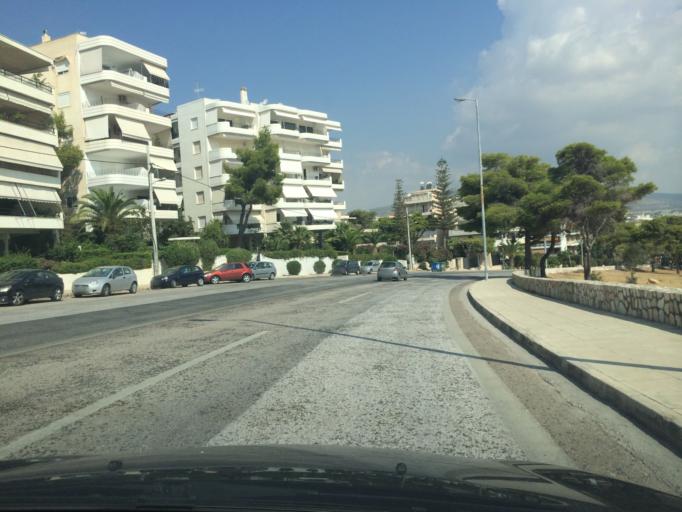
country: GR
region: Attica
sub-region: Nomarchia Anatolikis Attikis
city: Vouliagmeni
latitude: 37.8104
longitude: 23.7997
